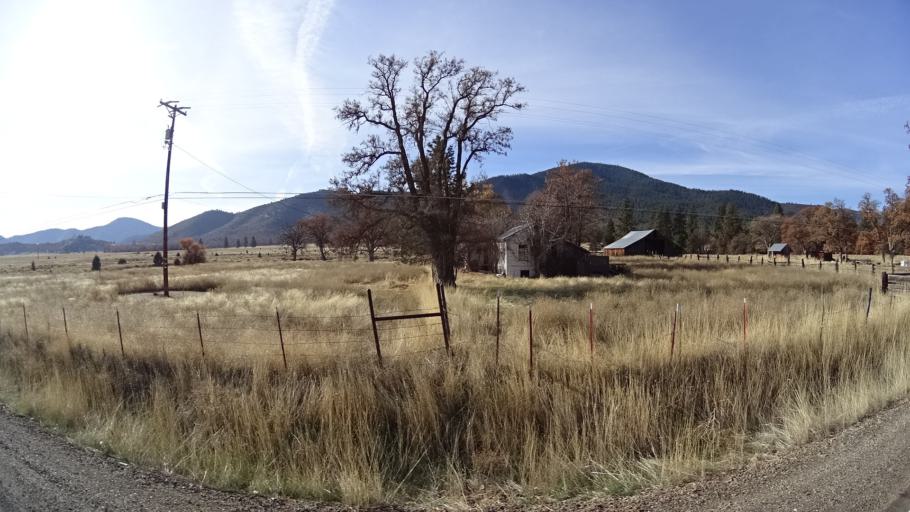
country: US
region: California
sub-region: Siskiyou County
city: Montague
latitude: 41.6574
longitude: -122.5854
